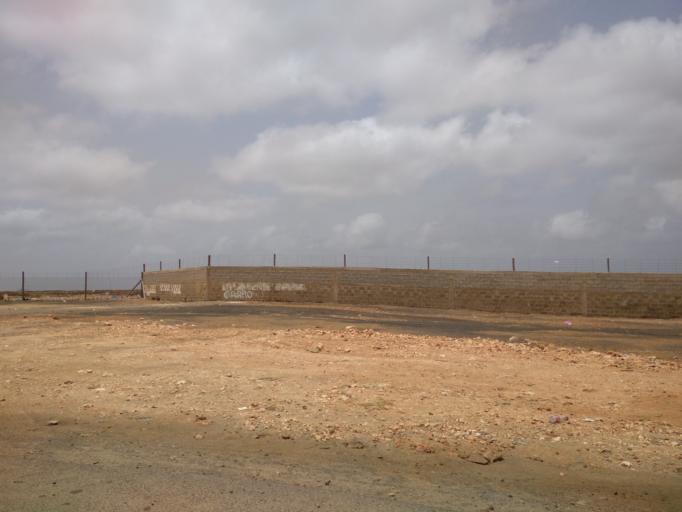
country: CV
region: Sal
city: Espargos
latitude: 16.7526
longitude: -22.9466
